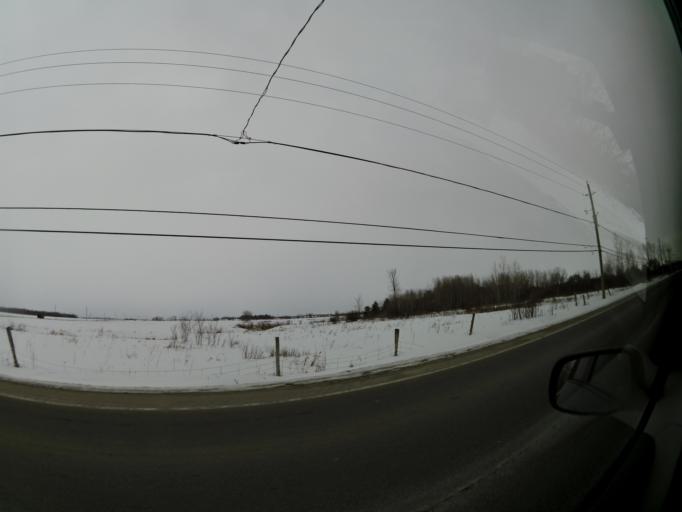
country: CA
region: Ontario
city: Clarence-Rockland
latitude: 45.4346
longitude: -75.4727
